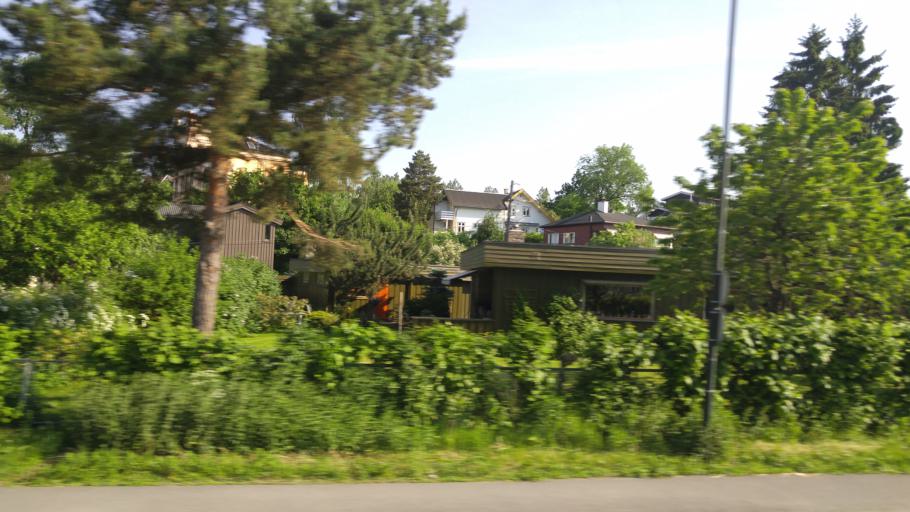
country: NO
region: Akershus
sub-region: Baerum
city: Sandvika
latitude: 59.8933
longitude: 10.5542
